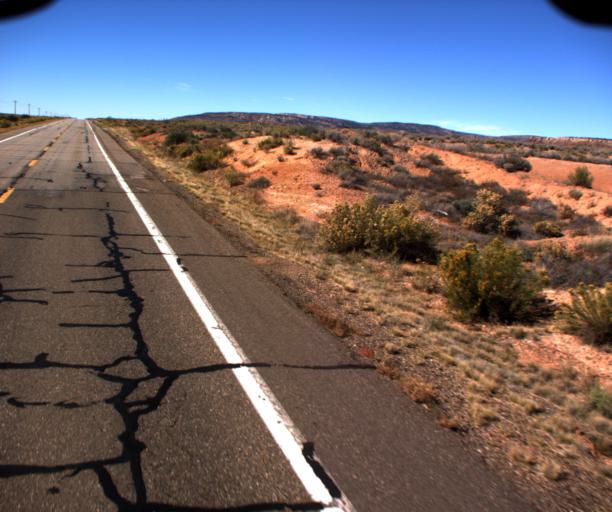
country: US
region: Arizona
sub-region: Coconino County
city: Fredonia
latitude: 36.8775
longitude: -112.6543
